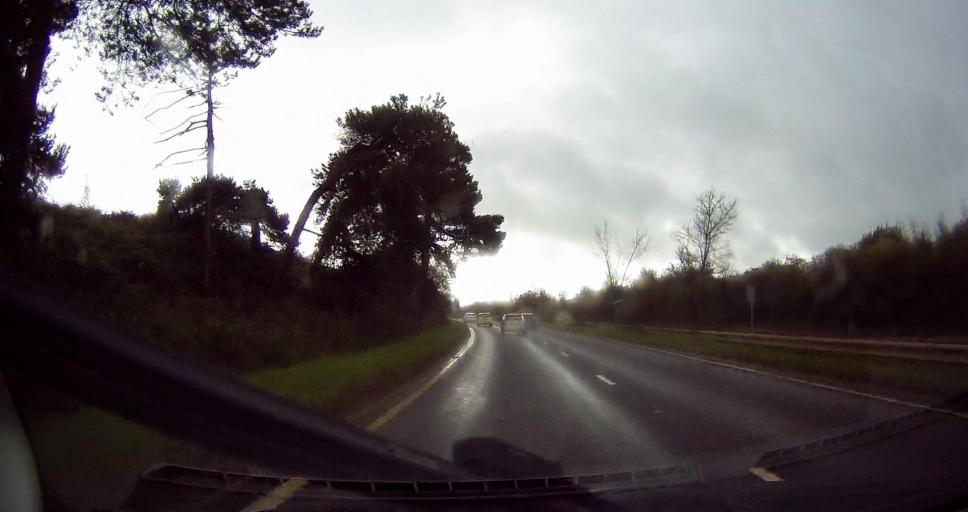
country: GB
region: England
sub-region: Staffordshire
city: Shenstone
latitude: 52.6169
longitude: -1.7984
